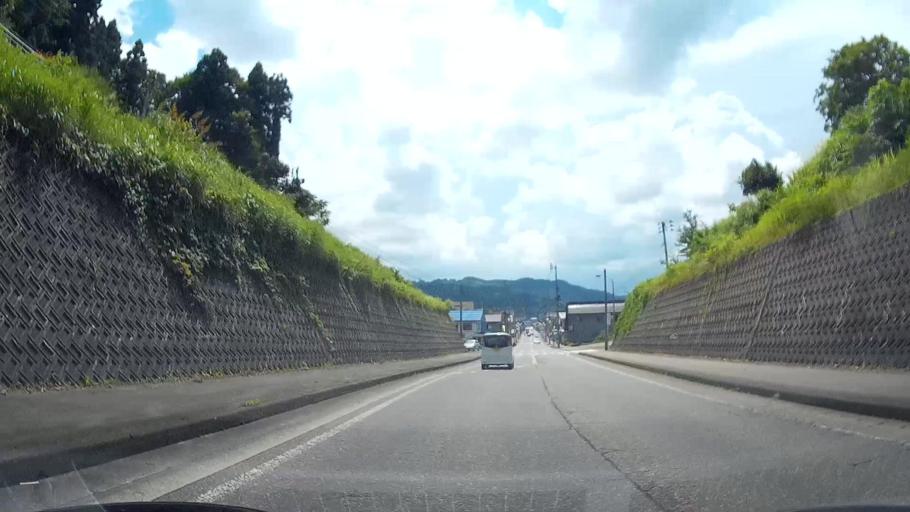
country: JP
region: Niigata
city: Tokamachi
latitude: 37.0173
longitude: 138.6551
